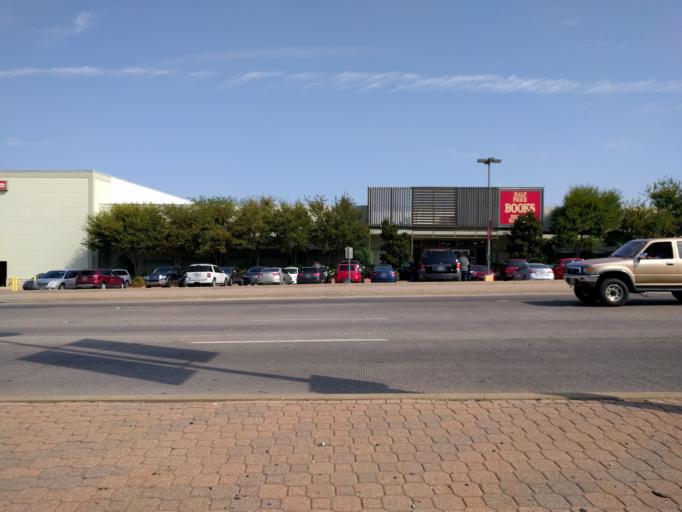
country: US
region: Texas
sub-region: Dallas County
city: University Park
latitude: 32.8655
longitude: -96.7648
